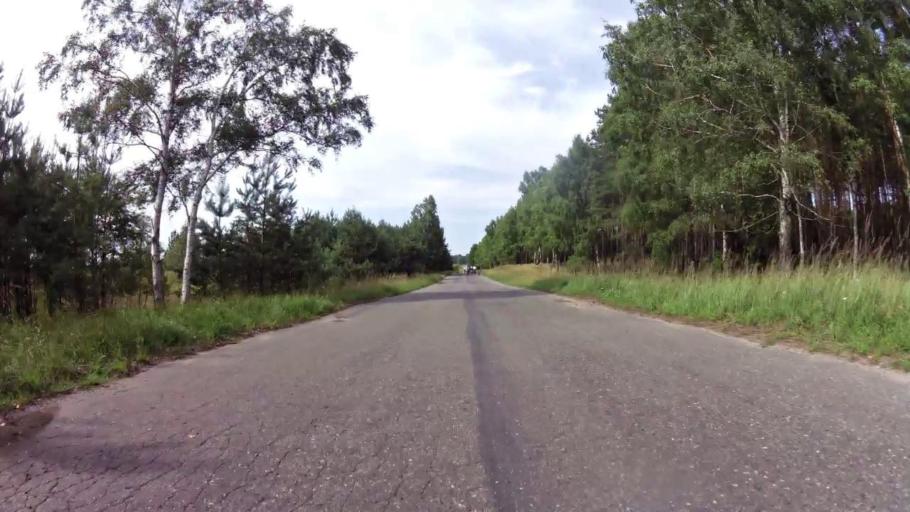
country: PL
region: West Pomeranian Voivodeship
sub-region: Powiat stargardzki
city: Insko
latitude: 53.4048
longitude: 15.6014
